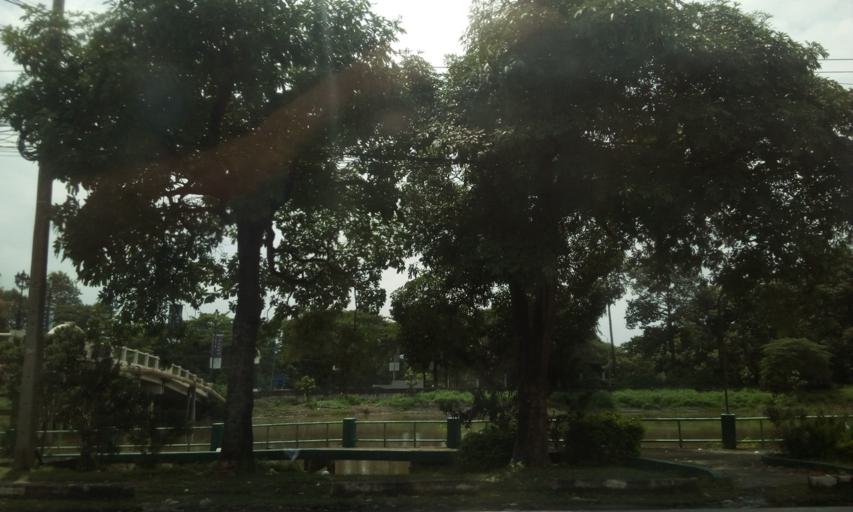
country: TH
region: Pathum Thani
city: Thanyaburi
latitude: 14.0061
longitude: 100.7005
